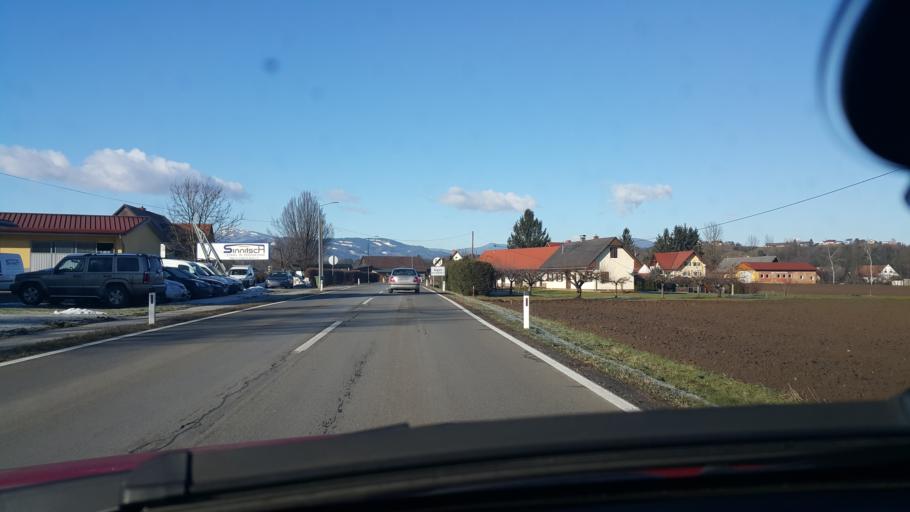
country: AT
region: Styria
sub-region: Politischer Bezirk Deutschlandsberg
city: Sankt Martin im Sulmtal
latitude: 46.7621
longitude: 15.2845
